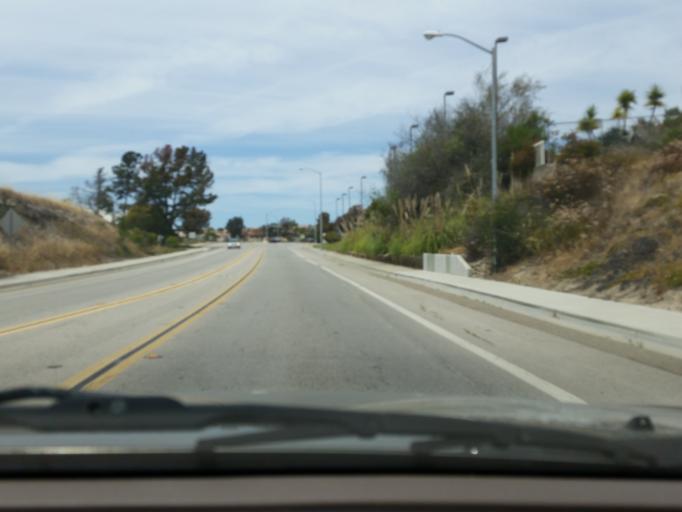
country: US
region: California
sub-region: San Luis Obispo County
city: Grover Beach
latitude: 35.1335
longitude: -120.6221
